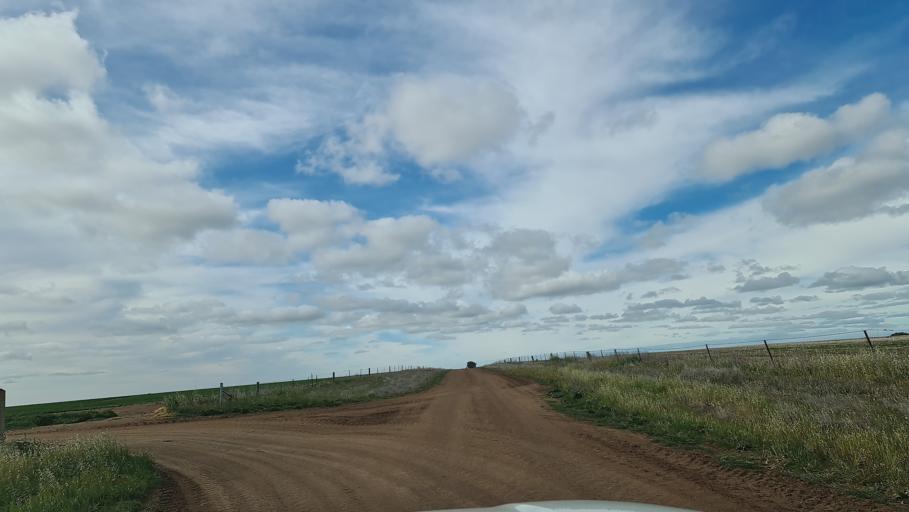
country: AU
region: Victoria
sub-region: Horsham
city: Horsham
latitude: -36.6313
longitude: 142.4190
